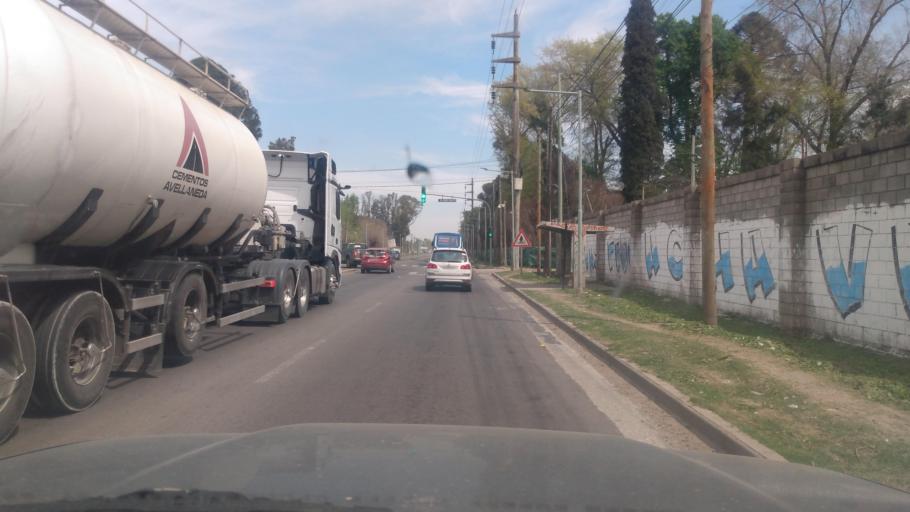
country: AR
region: Buenos Aires
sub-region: Partido de Pilar
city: Pilar
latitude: -34.4393
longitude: -58.8955
